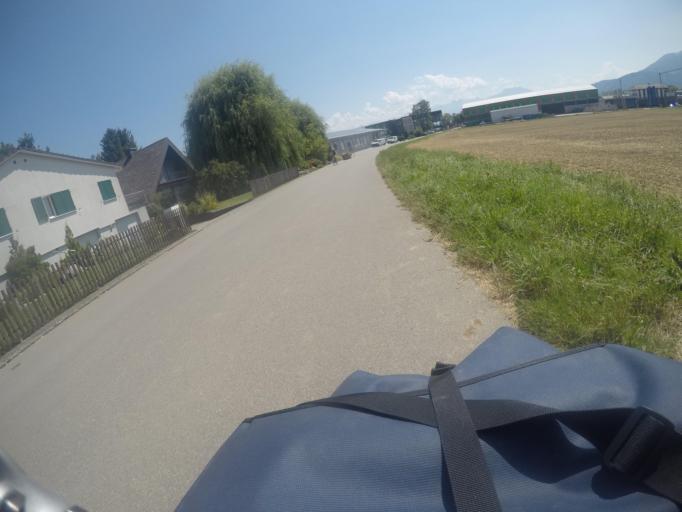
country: CH
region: Saint Gallen
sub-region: Wahlkreis Rheintal
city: Altstatten
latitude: 47.3699
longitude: 9.5583
